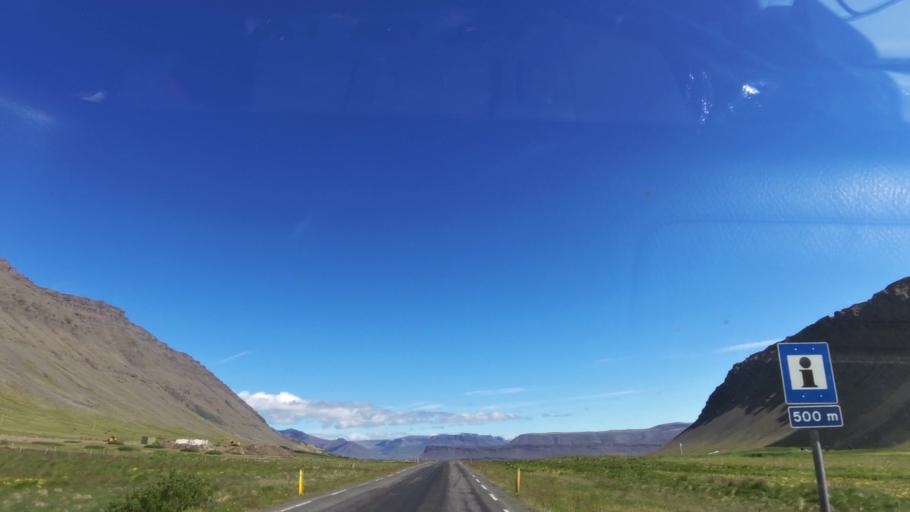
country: IS
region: Westfjords
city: Isafjoerdur
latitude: 65.6706
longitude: -23.6258
